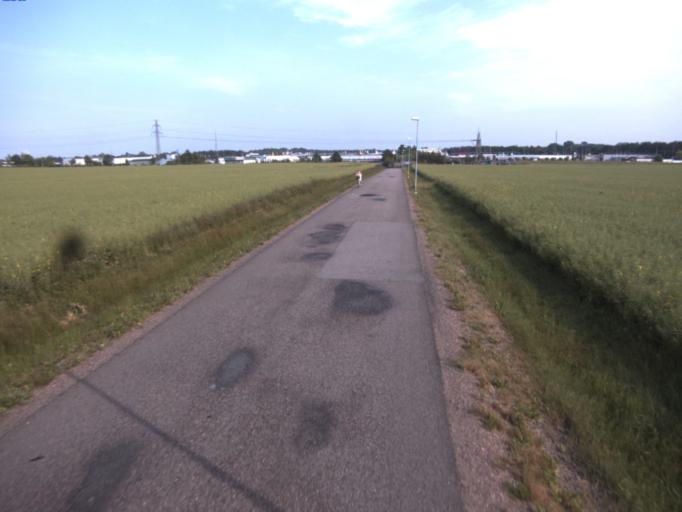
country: SE
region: Skane
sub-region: Helsingborg
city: Odakra
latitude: 56.0784
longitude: 12.7079
